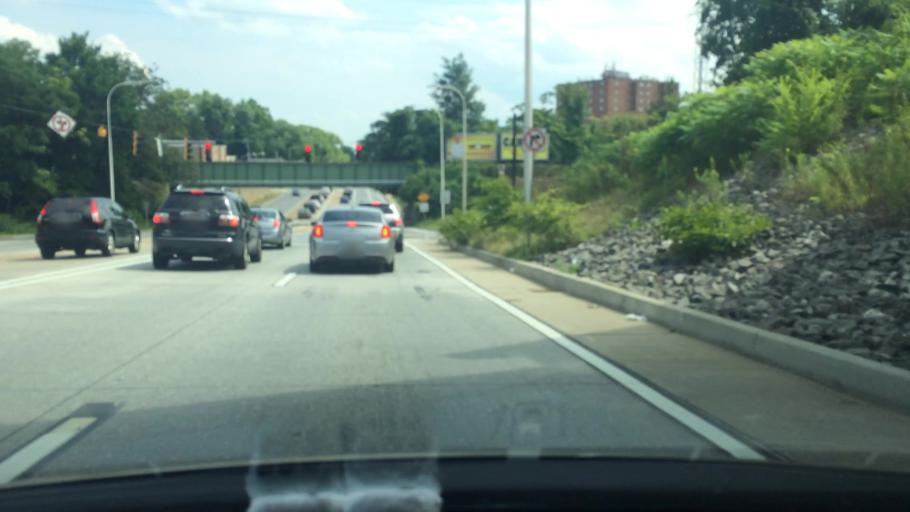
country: US
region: Delaware
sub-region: New Castle County
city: Wilmington
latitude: 39.7656
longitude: -75.5429
